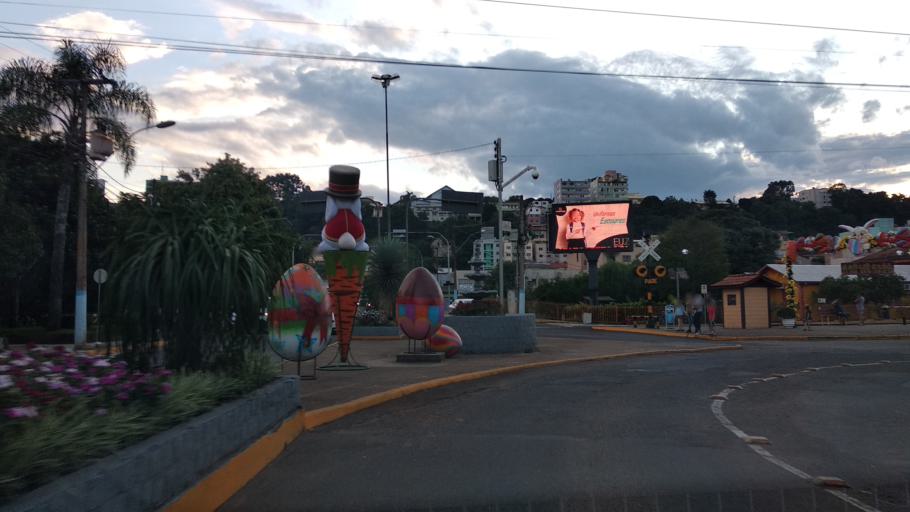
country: BR
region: Santa Catarina
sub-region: Videira
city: Videira
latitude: -27.0052
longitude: -51.1545
